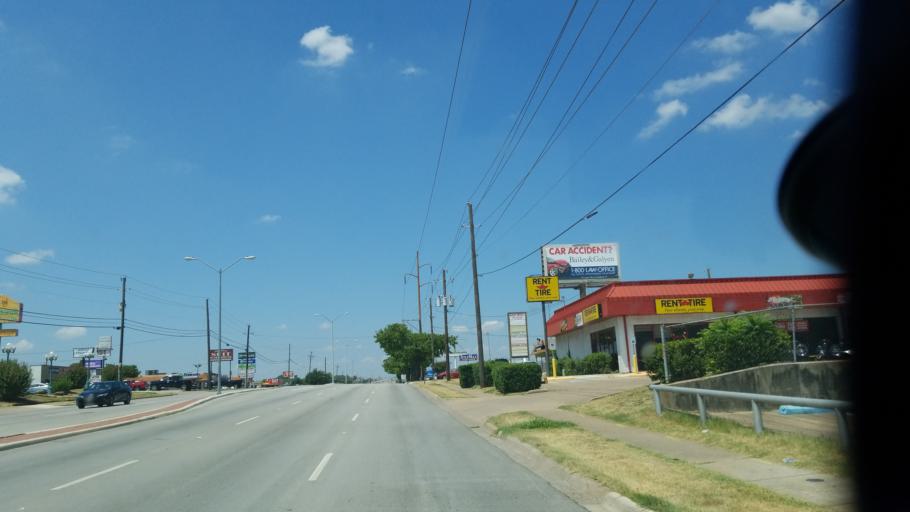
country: US
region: Texas
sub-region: Dallas County
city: Duncanville
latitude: 32.6622
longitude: -96.8846
